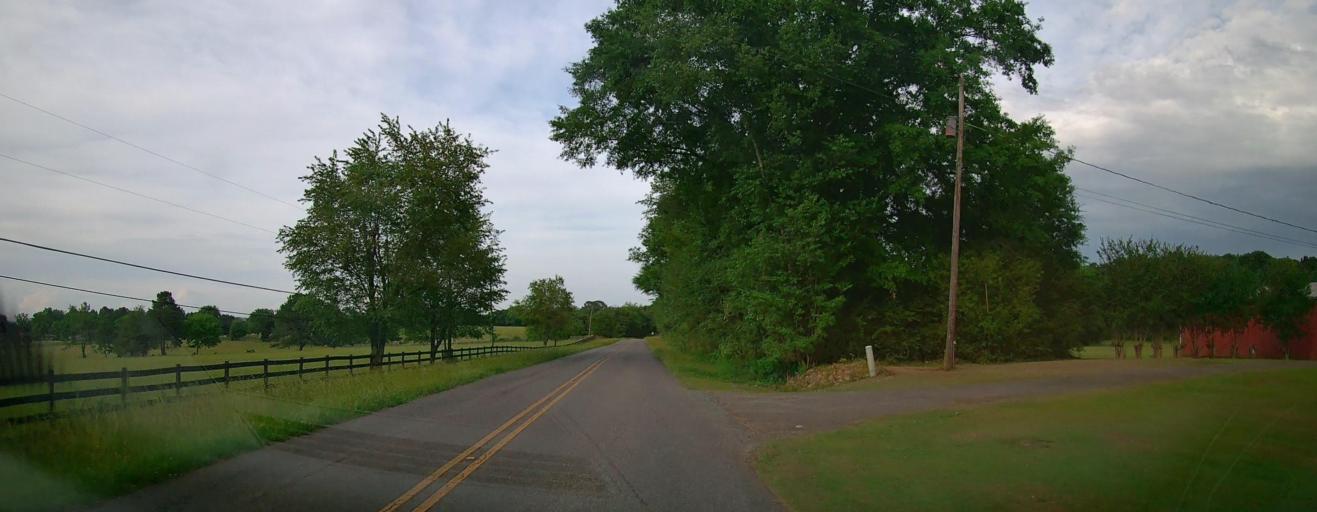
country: US
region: Alabama
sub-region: Calhoun County
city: Oxford
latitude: 33.5780
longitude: -85.8349
